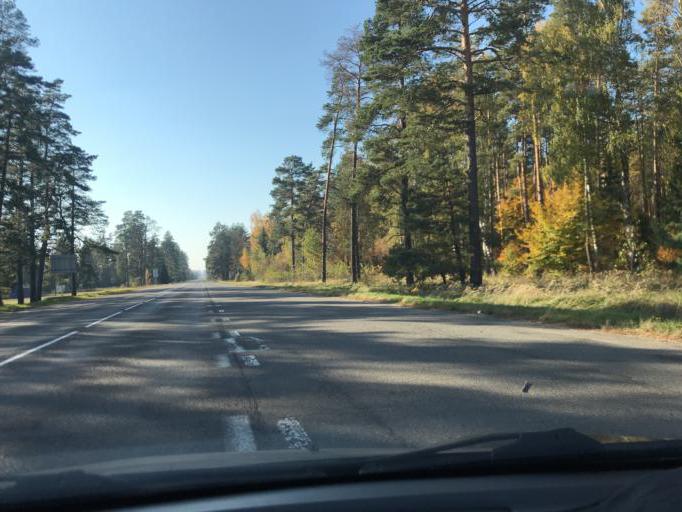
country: BY
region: Mogilev
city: Hlusha
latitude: 53.0866
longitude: 28.8454
